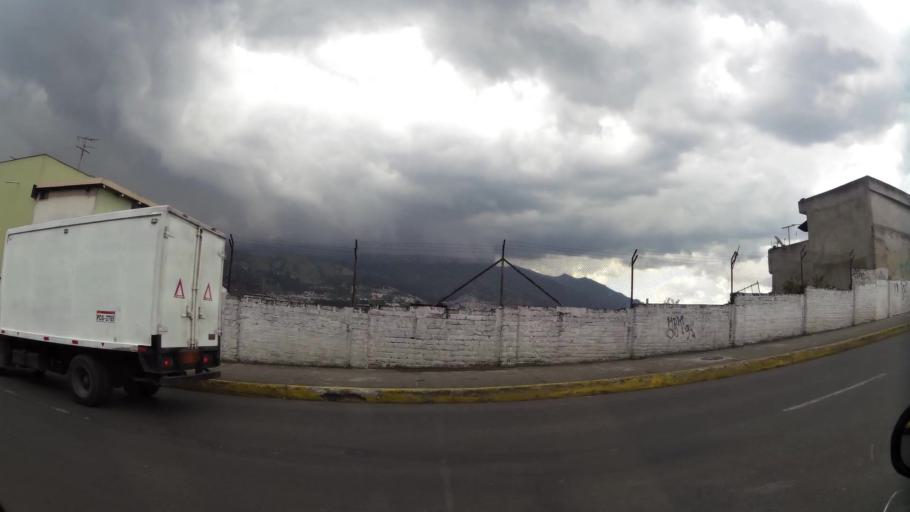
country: EC
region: Pichincha
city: Quito
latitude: -0.2463
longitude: -78.5051
